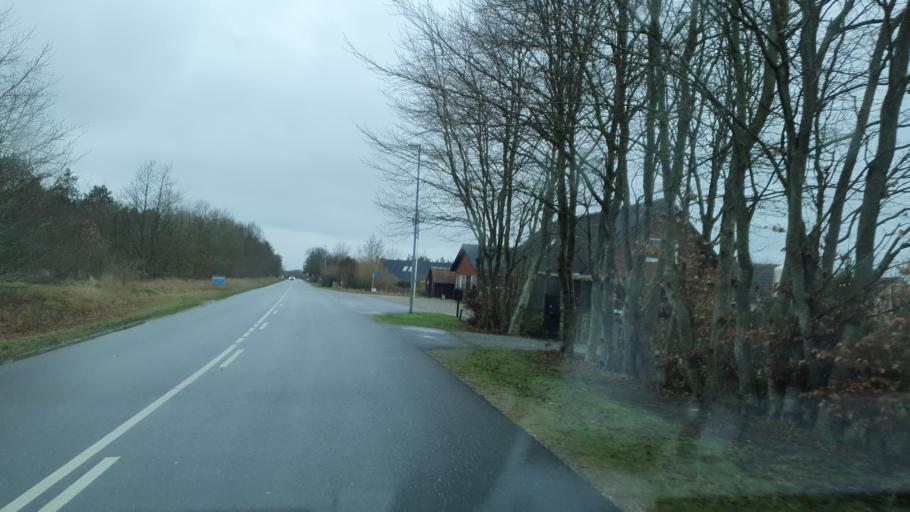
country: DK
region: North Denmark
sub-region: Jammerbugt Kommune
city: Fjerritslev
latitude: 57.1312
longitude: 9.1330
